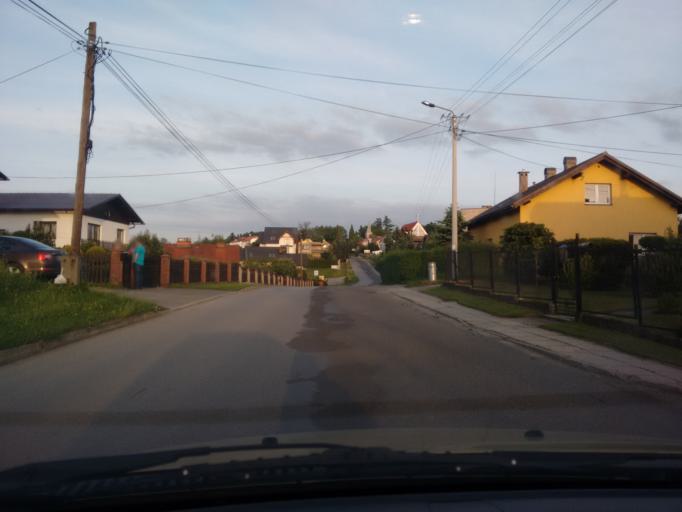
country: PL
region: Silesian Voivodeship
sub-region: Powiat cieszynski
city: Puncow
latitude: 49.7384
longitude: 18.6578
